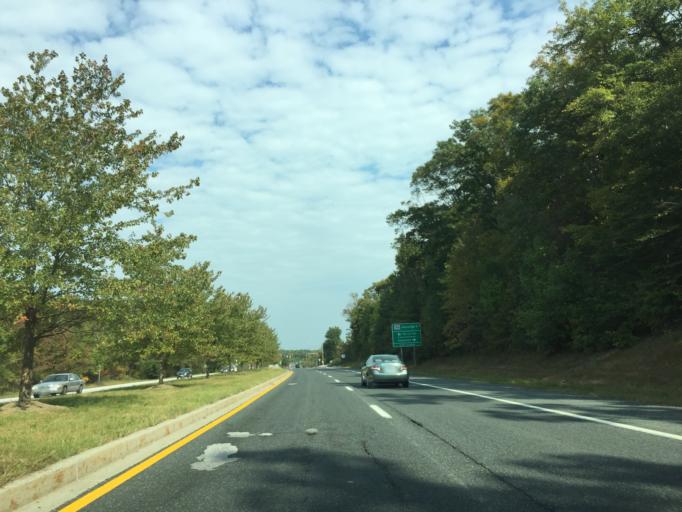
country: US
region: Maryland
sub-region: Harford County
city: Edgewood
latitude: 39.4306
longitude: -76.3076
